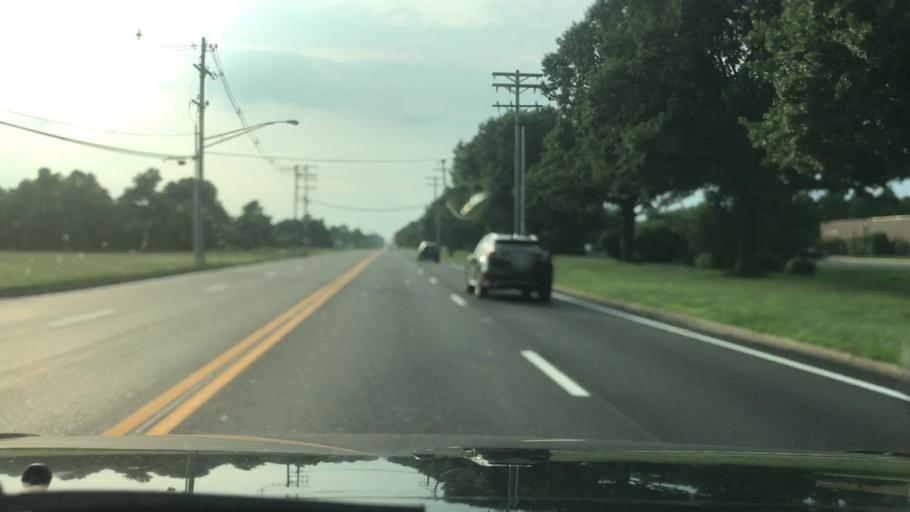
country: US
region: New Jersey
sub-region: Ocean County
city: Leisure Village
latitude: 40.0692
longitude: -74.1680
